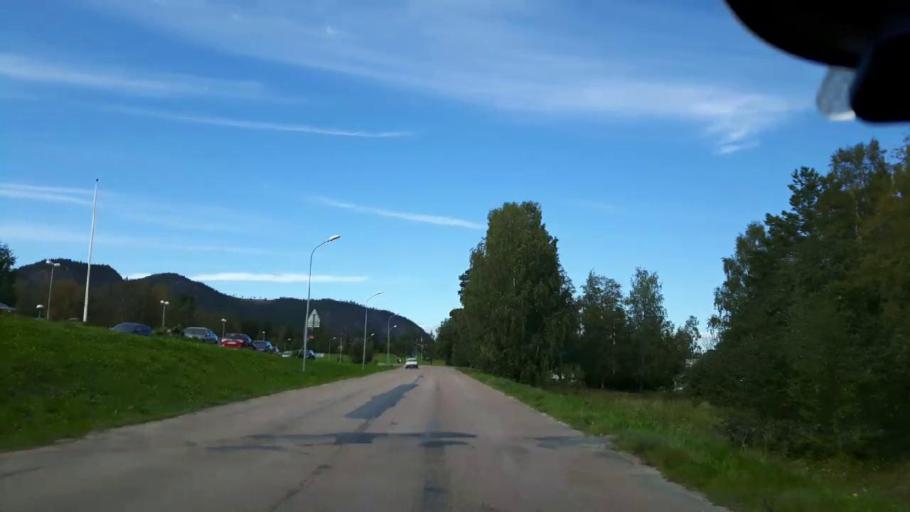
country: SE
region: Jaemtland
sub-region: Ragunda Kommun
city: Hammarstrand
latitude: 63.1142
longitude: 16.3493
